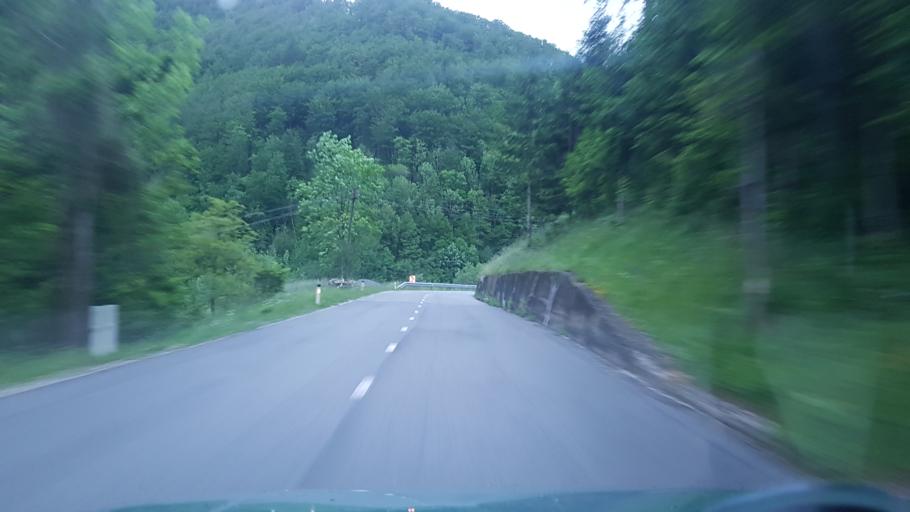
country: SI
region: Cerkno
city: Cerkno
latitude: 46.1724
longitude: 13.9108
